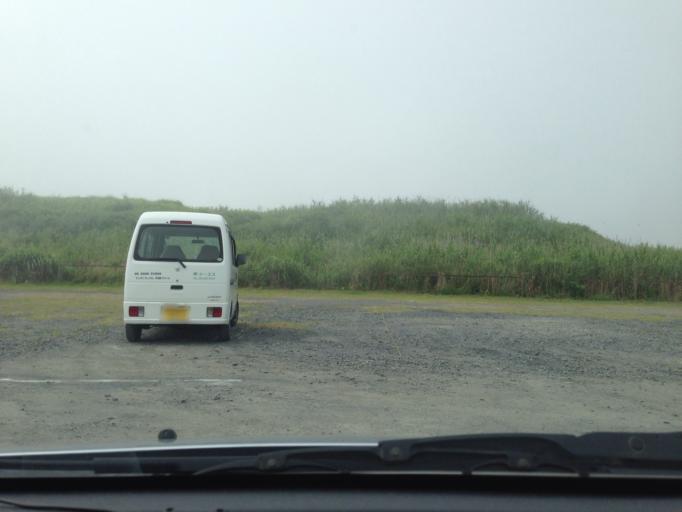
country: JP
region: Ibaraki
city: Oarai
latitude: 36.3460
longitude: 140.6064
